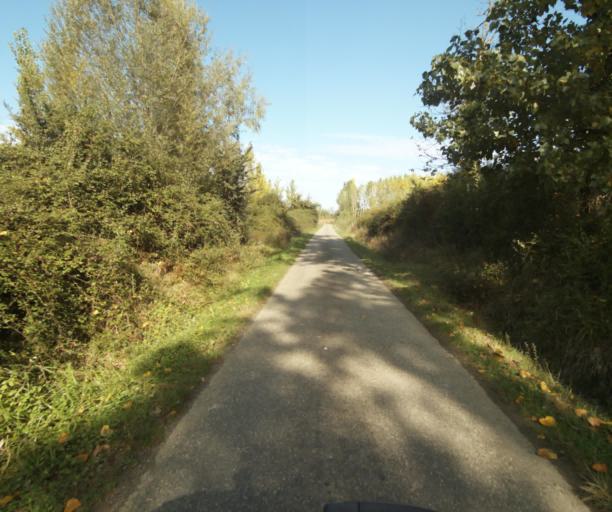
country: FR
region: Midi-Pyrenees
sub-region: Departement du Tarn-et-Garonne
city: Finhan
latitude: 43.9089
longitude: 1.2149
